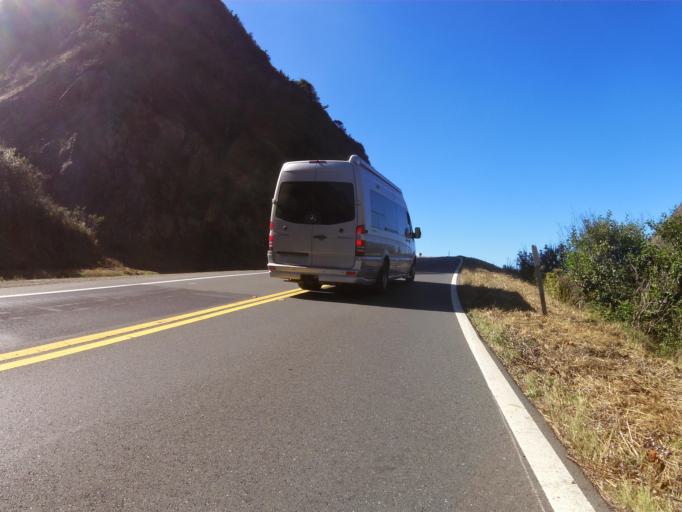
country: US
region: California
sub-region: Mendocino County
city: Fort Bragg
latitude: 39.6132
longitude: -123.7791
